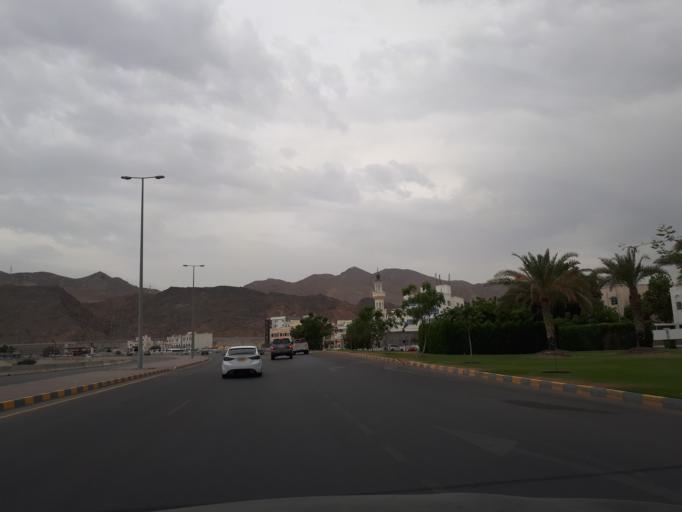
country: OM
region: Muhafazat Masqat
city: Bawshar
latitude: 23.5953
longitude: 58.4573
